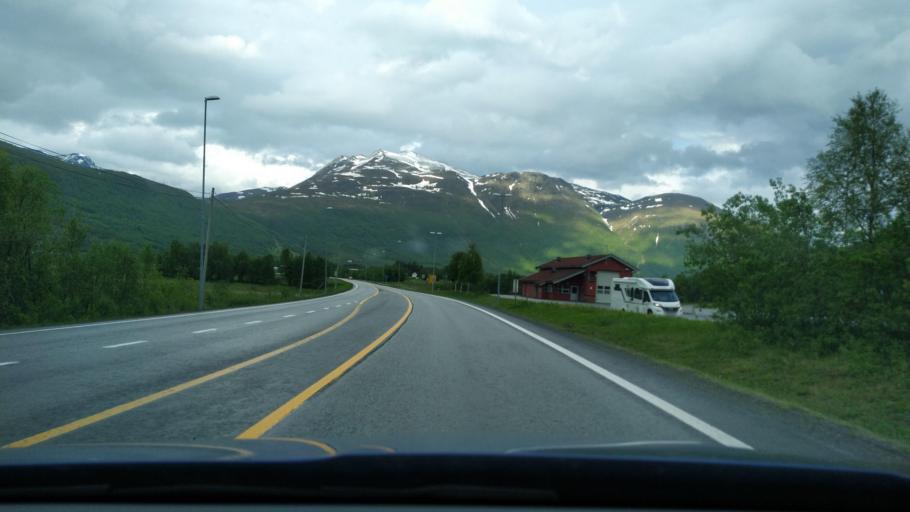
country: NO
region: Troms
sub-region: Balsfjord
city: Storsteinnes
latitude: 69.2130
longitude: 19.5369
